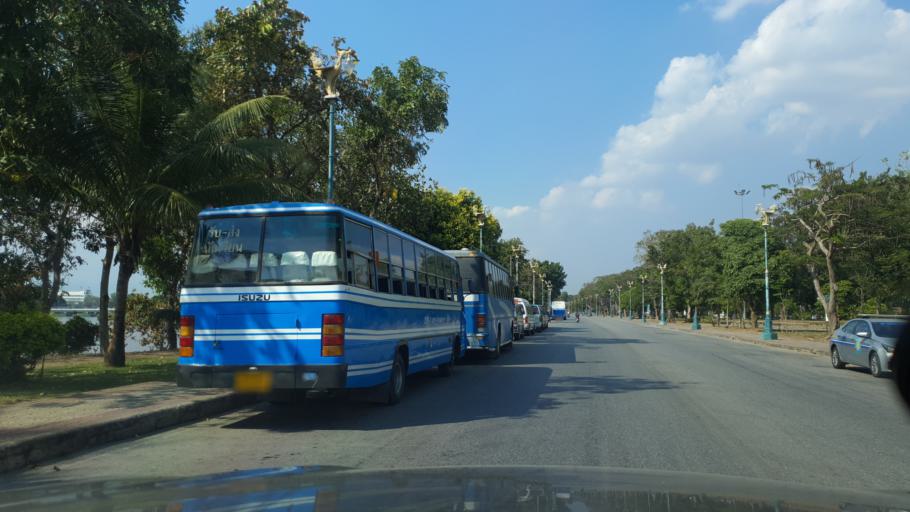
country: TH
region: Tak
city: Tak
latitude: 16.8792
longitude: 99.1204
